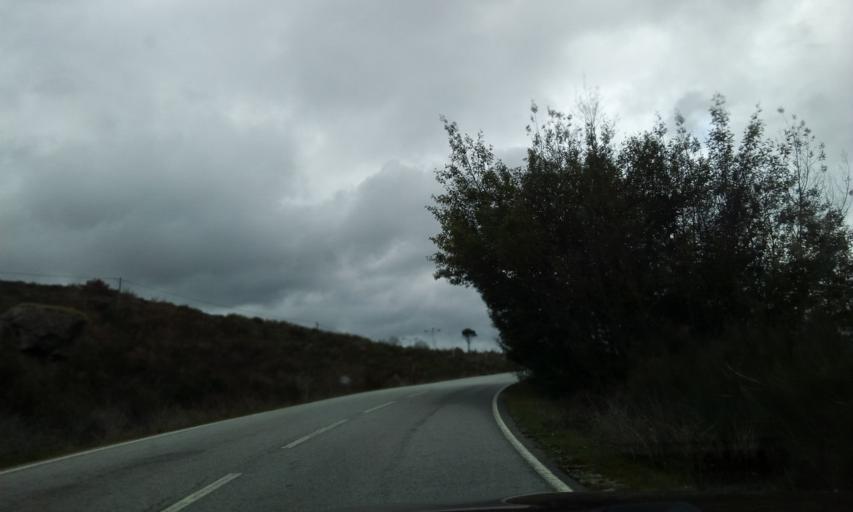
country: PT
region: Viseu
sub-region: Viseu
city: Rio de Loba
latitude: 40.6089
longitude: -7.8662
